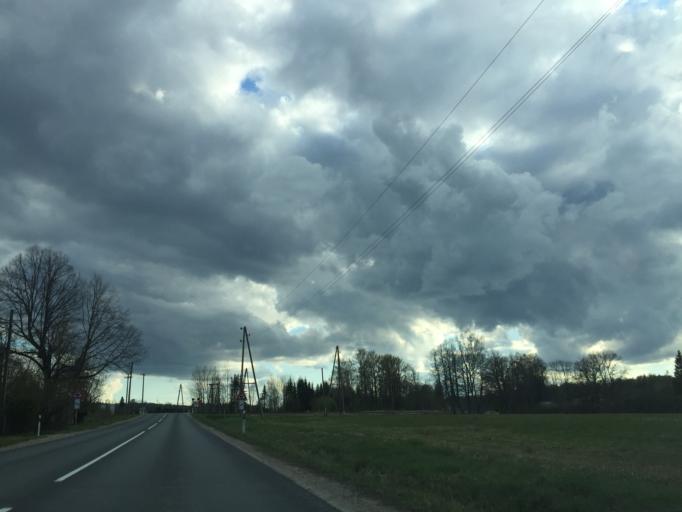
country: LV
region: Priekuli
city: Priekuli
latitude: 57.3541
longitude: 25.3587
